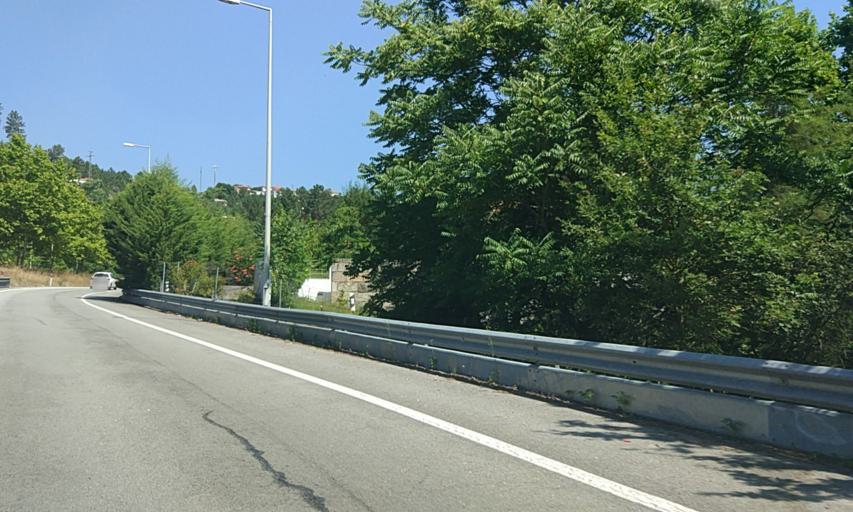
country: PT
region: Porto
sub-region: Amarante
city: Amarante
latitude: 41.2628
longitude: -8.1090
